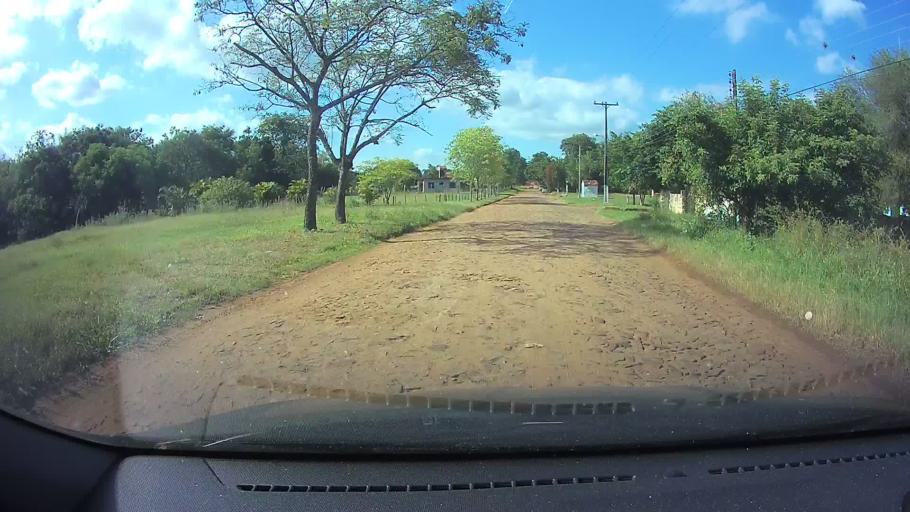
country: PY
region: Central
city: Limpio
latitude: -25.2495
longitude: -57.4702
